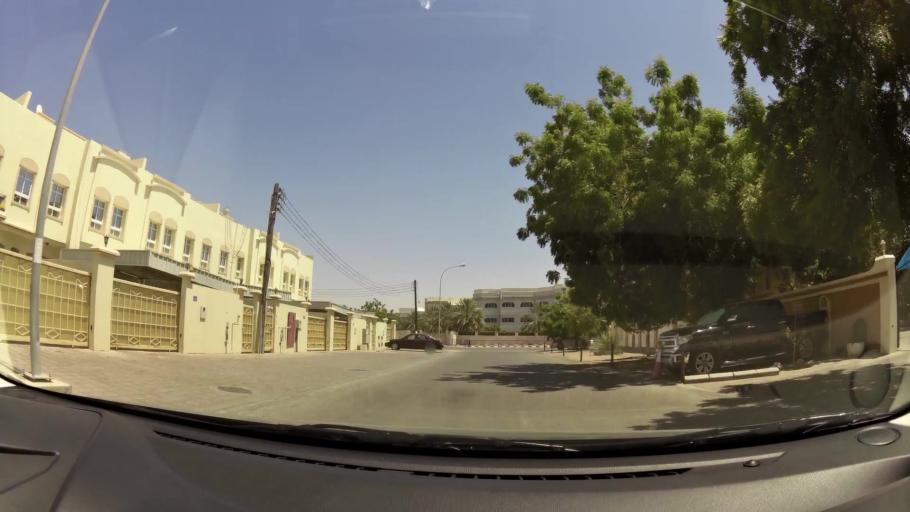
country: OM
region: Muhafazat Masqat
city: As Sib al Jadidah
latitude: 23.6184
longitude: 58.2302
